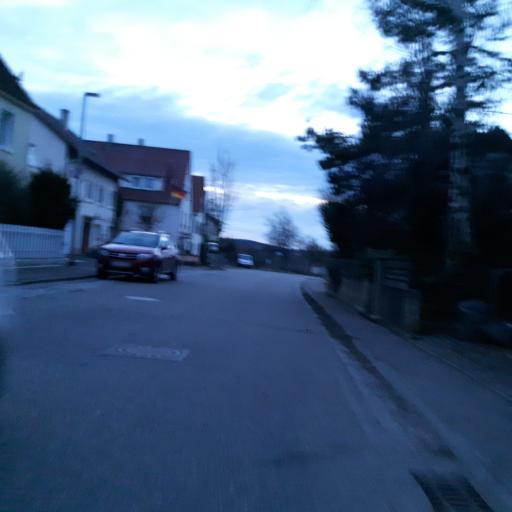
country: DE
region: Baden-Wuerttemberg
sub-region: Regierungsbezirk Stuttgart
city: Hessigheim
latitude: 48.9936
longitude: 9.1827
